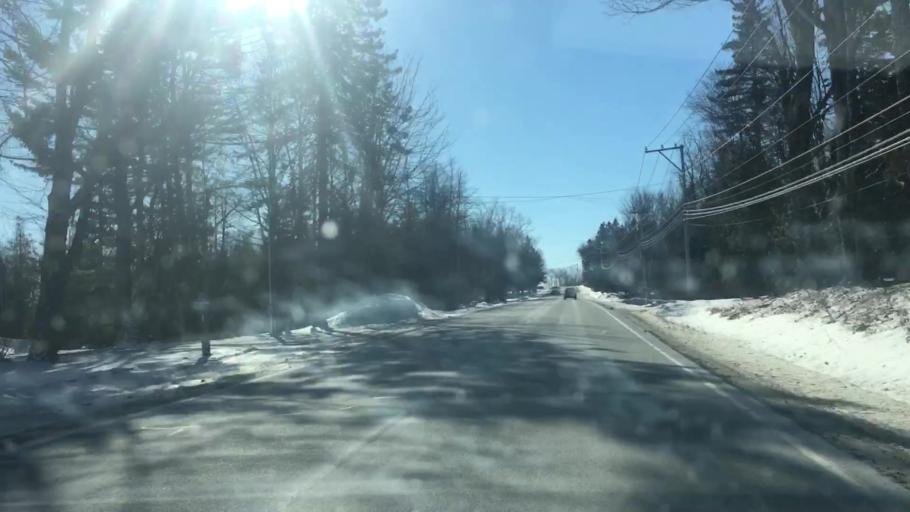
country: US
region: Maine
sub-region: Hancock County
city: Ellsworth
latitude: 44.5129
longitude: -68.4359
